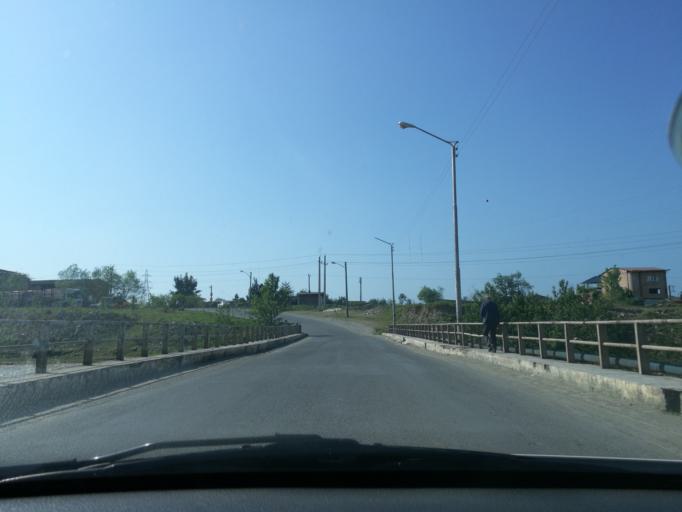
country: IR
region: Mazandaran
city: Chalus
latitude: 36.6592
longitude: 51.4368
